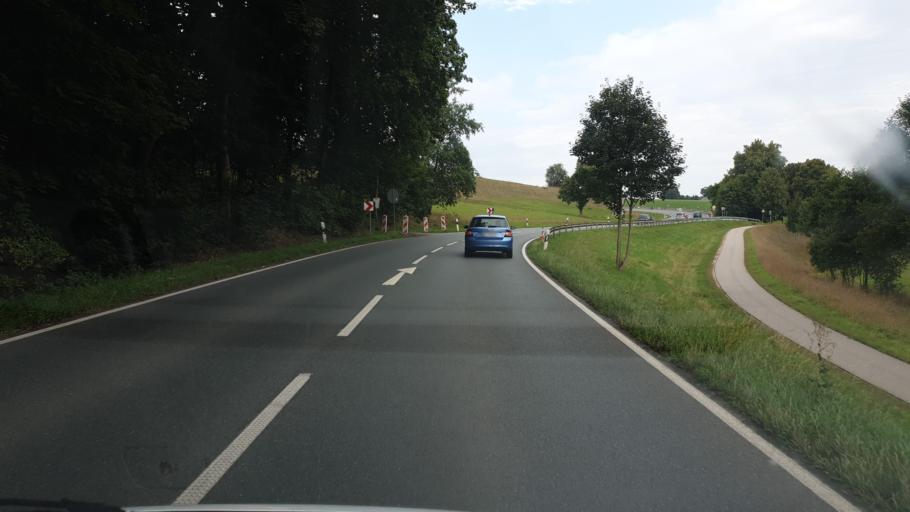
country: DE
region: Saxony
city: Lengenfeld
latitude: 50.5820
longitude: 12.3537
